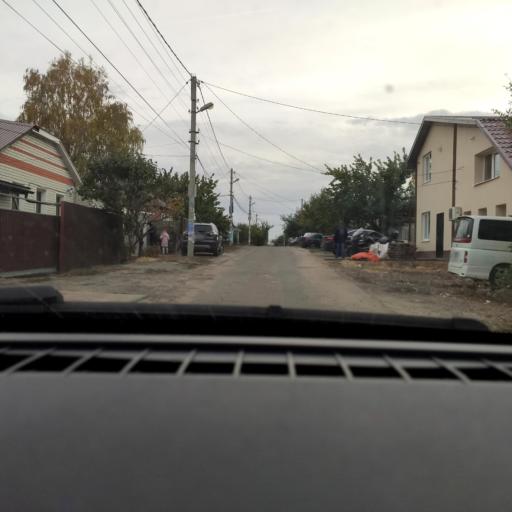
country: RU
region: Voronezj
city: Voronezh
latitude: 51.6720
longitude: 39.2645
